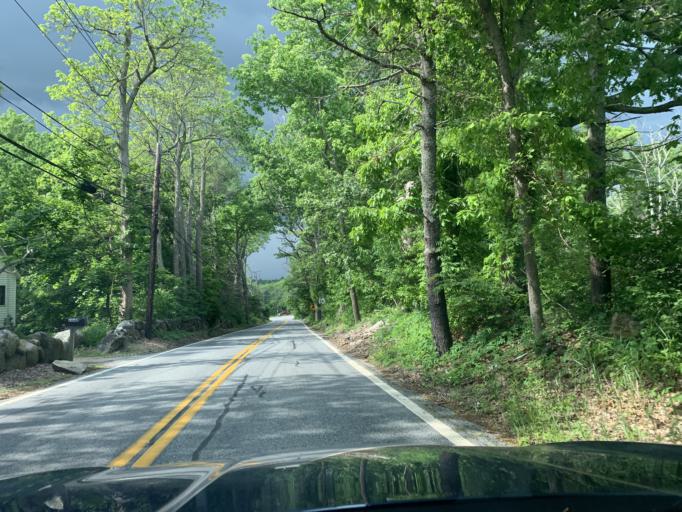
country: US
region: Rhode Island
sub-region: Kent County
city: Coventry
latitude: 41.7055
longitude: -71.7563
